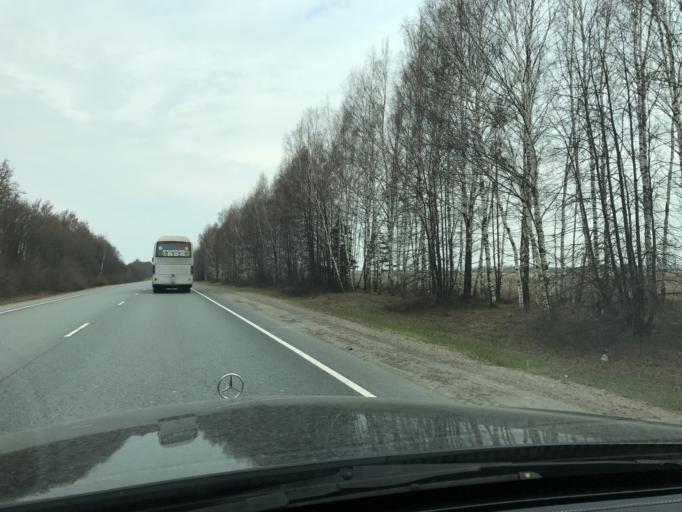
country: RU
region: Vladimir
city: Suzdal'
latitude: 56.3669
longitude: 40.4641
